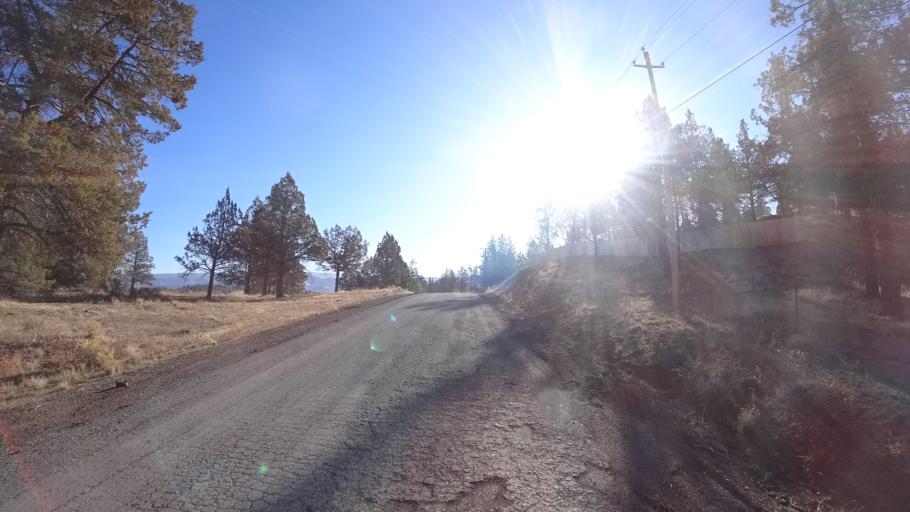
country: US
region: California
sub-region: Siskiyou County
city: Montague
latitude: 41.8895
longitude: -122.4330
